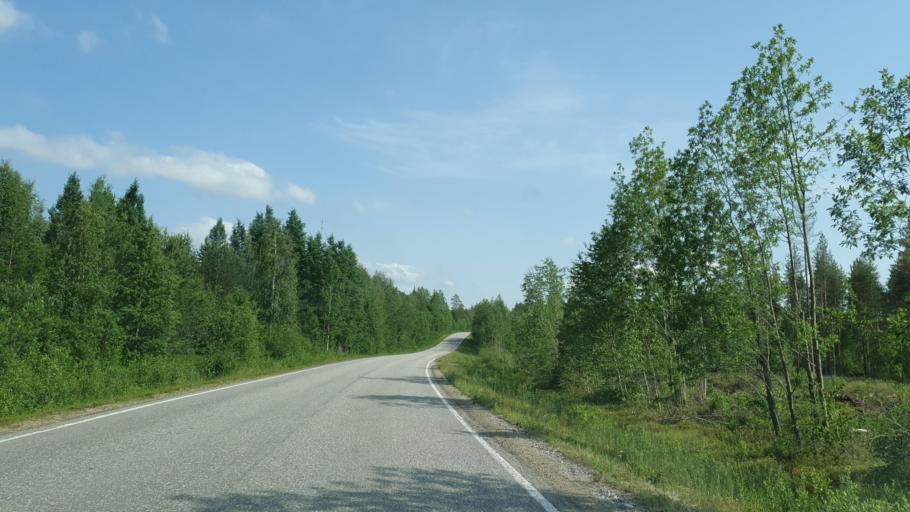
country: FI
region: Kainuu
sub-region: Kehys-Kainuu
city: Kuhmo
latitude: 64.1073
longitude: 29.7521
